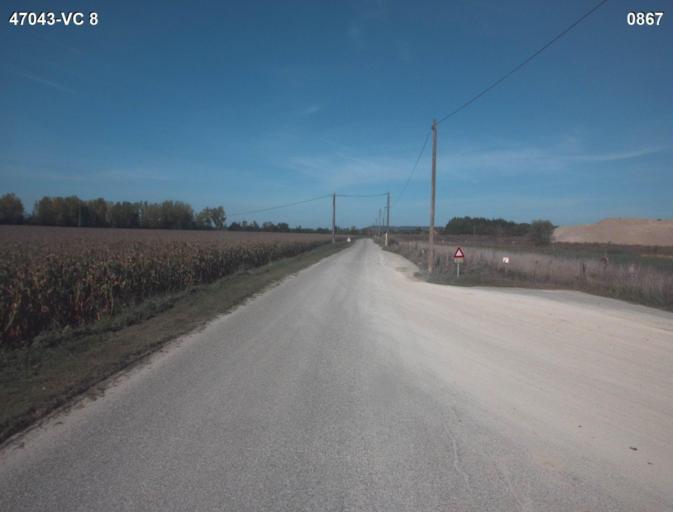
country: FR
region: Aquitaine
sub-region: Departement du Lot-et-Garonne
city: Damazan
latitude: 44.2772
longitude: 0.2915
